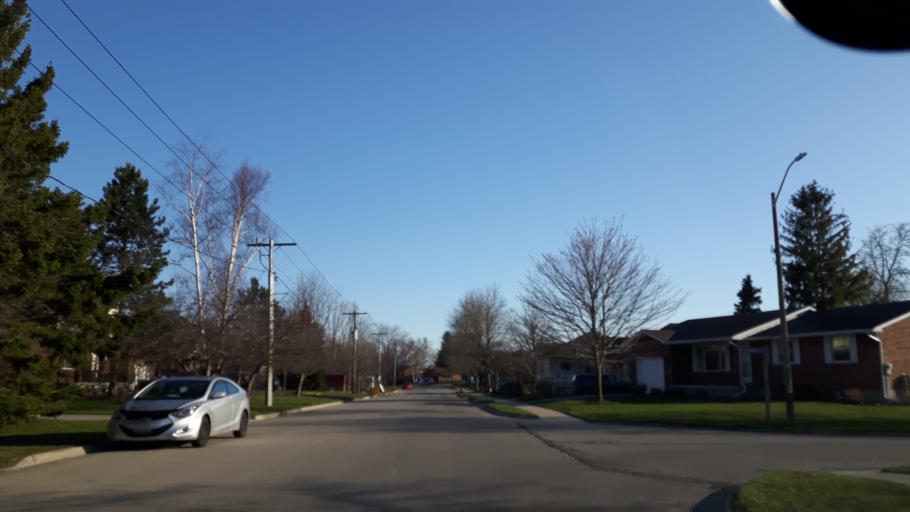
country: CA
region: Ontario
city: Goderich
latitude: 43.7325
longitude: -81.7111
